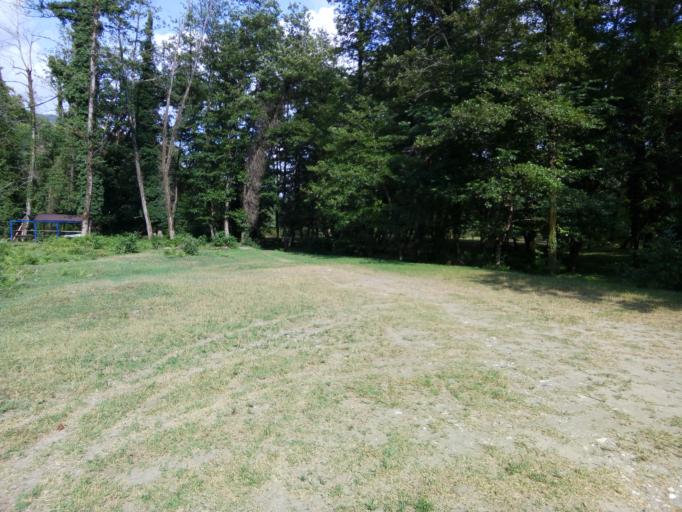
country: RU
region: Krasnodarskiy
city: Vardane
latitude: 43.8399
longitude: 39.5282
